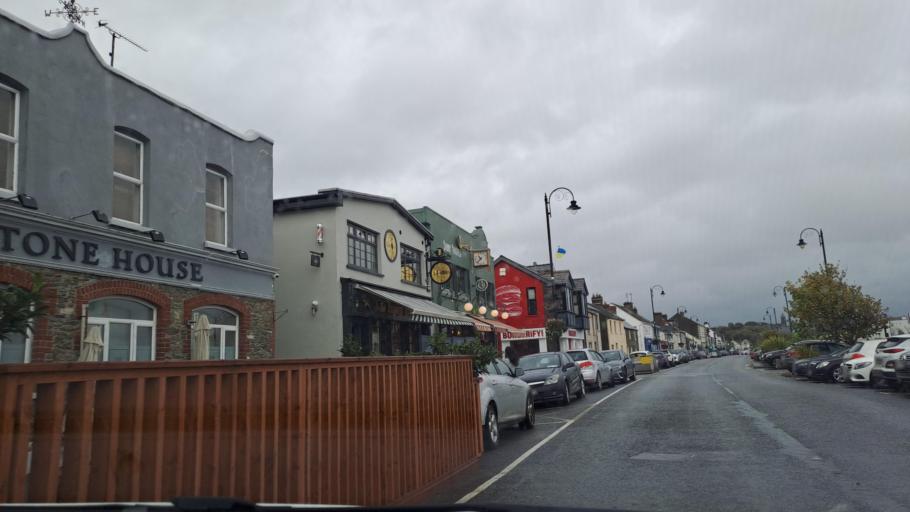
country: IE
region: Leinster
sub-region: Lu
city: Blackrock
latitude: 53.9609
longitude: -6.3672
